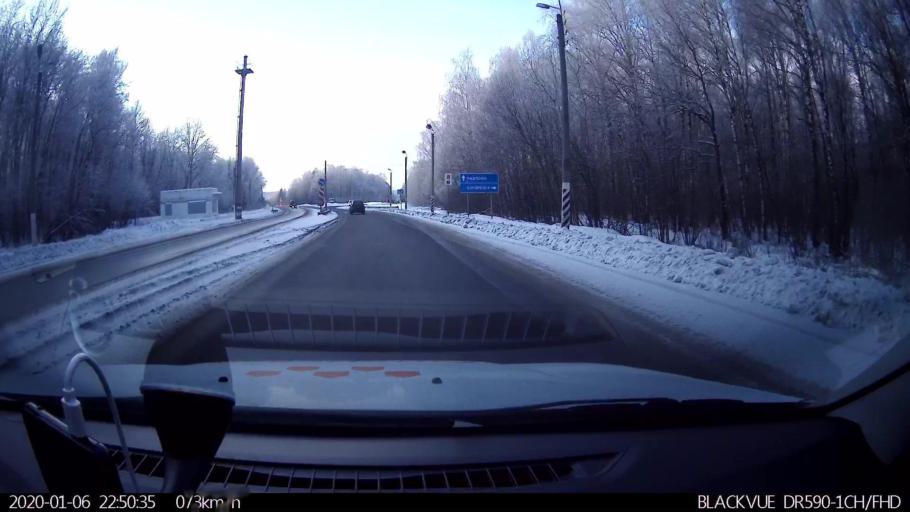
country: RU
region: Nizjnij Novgorod
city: Babino
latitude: 56.1334
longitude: 43.6136
